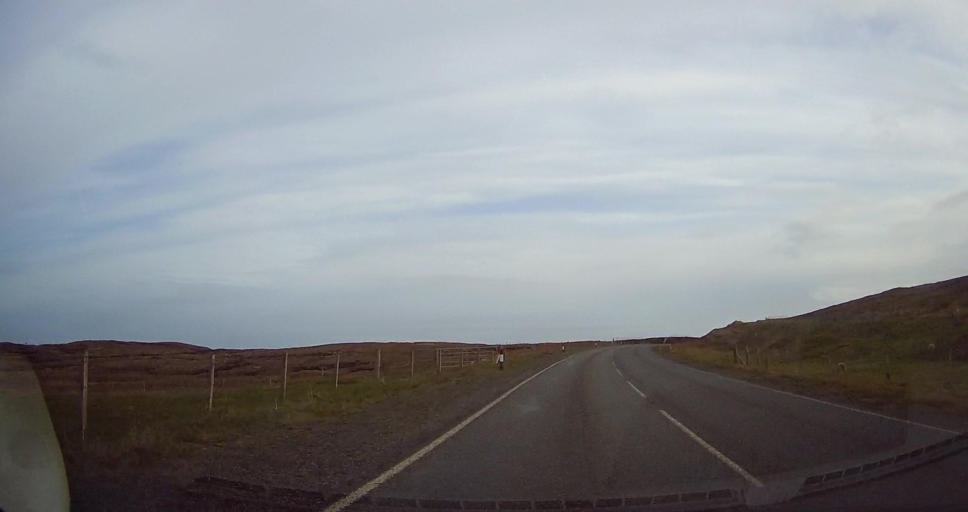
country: GB
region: Scotland
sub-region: Shetland Islands
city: Sandwick
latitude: 60.0916
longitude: -1.2283
